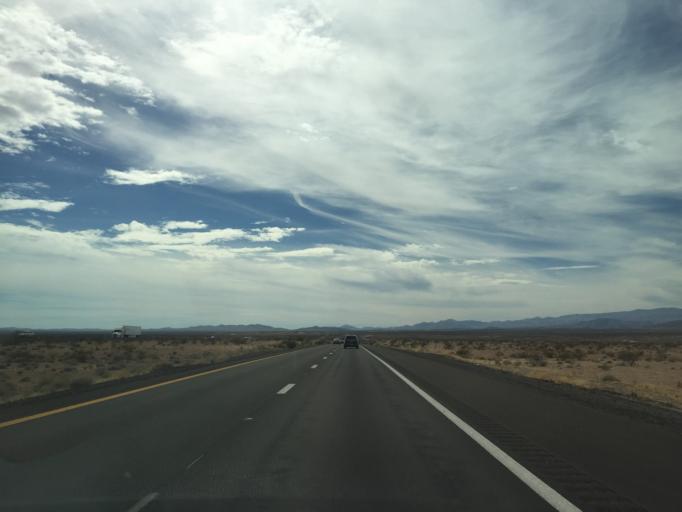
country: US
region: Nevada
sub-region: Clark County
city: Moapa Town
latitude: 36.5726
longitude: -114.6681
